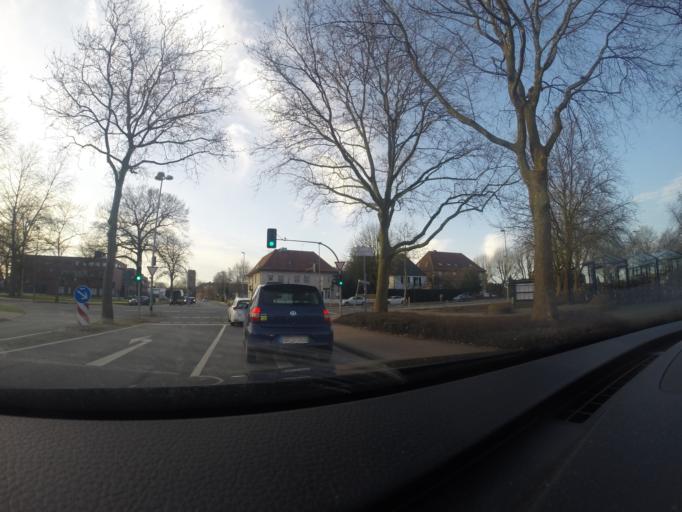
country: DE
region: North Rhine-Westphalia
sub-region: Regierungsbezirk Munster
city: Ahaus
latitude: 52.0825
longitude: 7.0154
